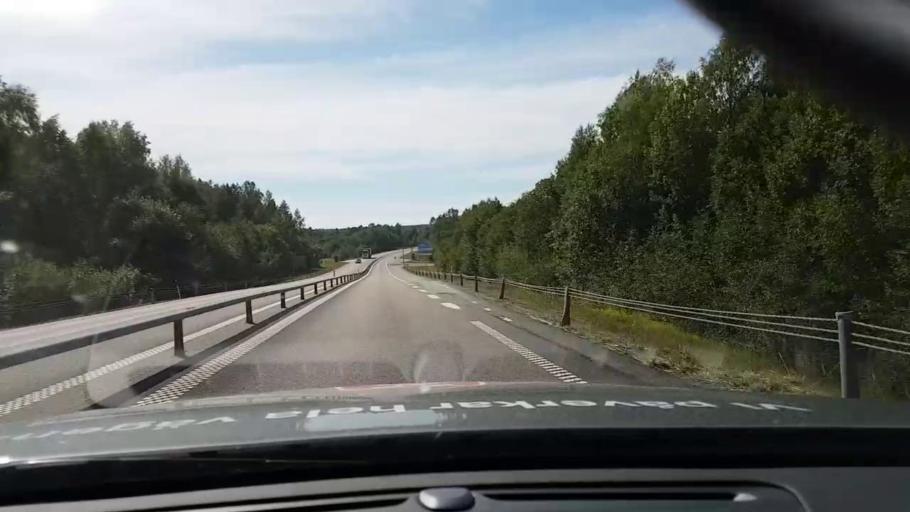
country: SE
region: Vaesternorrland
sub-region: OErnskoeldsviks Kommun
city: Husum
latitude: 63.3492
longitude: 19.1473
